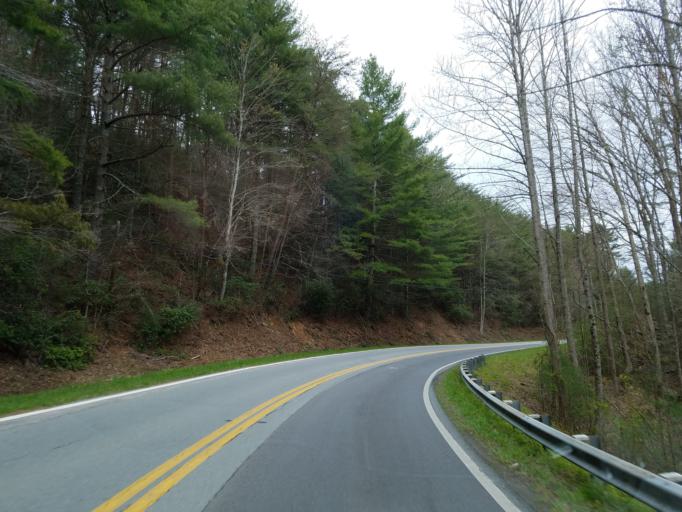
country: US
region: Georgia
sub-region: Fannin County
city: Blue Ridge
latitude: 34.8075
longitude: -84.2811
